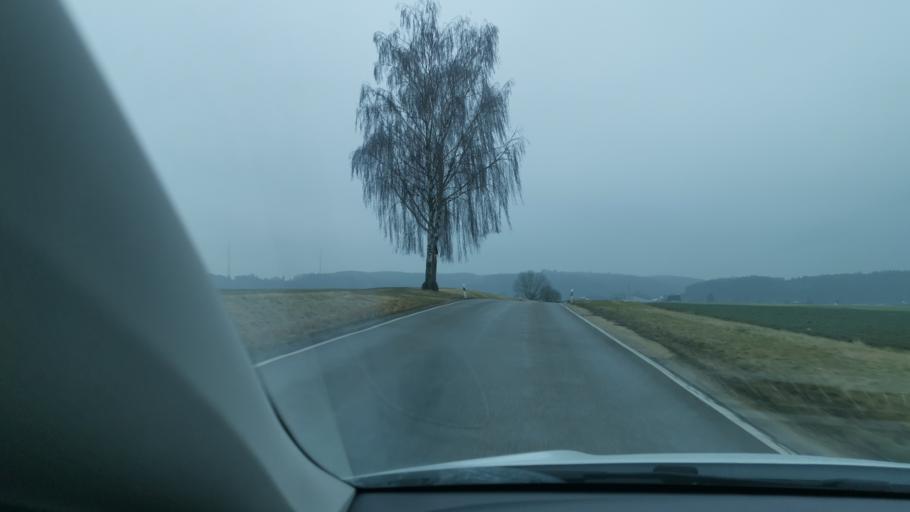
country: DE
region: Bavaria
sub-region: Swabia
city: Holzheim
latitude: 48.5903
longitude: 10.9428
